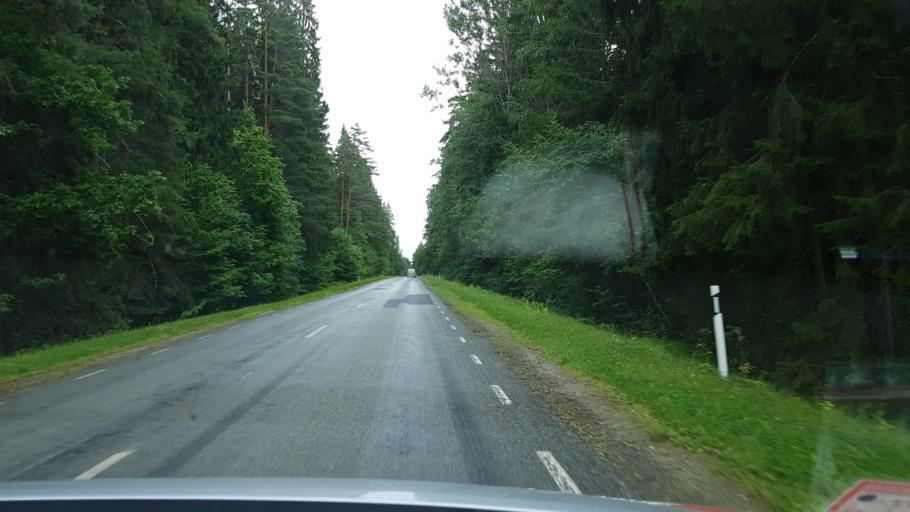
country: EE
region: Polvamaa
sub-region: Raepina vald
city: Rapina
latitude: 58.0798
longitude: 27.4297
